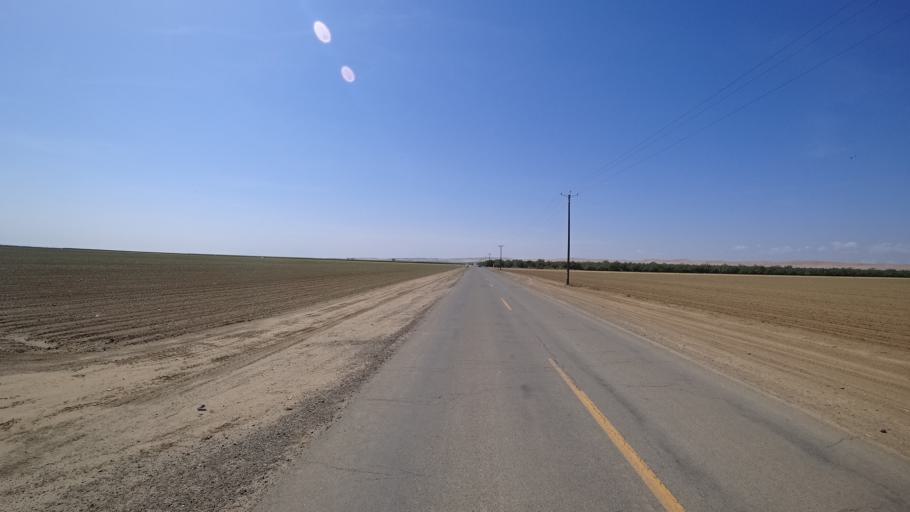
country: US
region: California
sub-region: Kings County
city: Kettleman City
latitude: 36.0742
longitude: -120.0036
